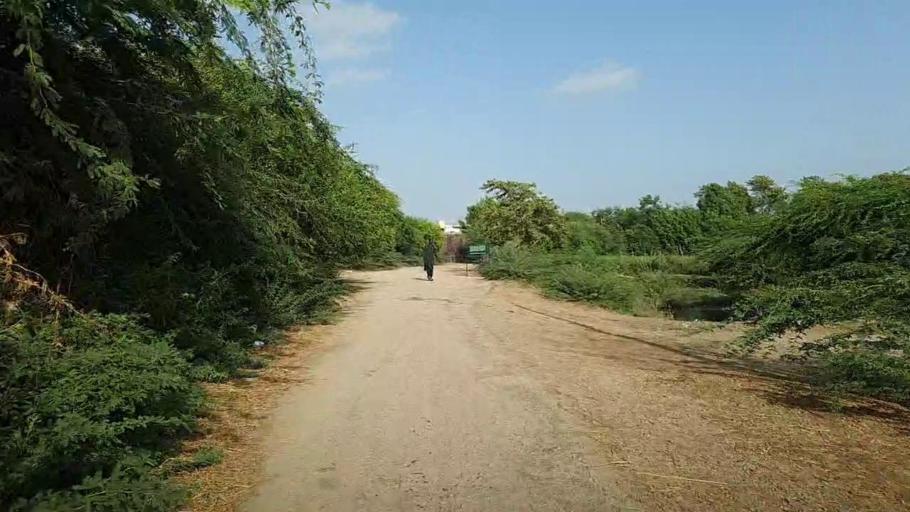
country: PK
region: Sindh
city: Kario
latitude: 24.6490
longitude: 68.4989
